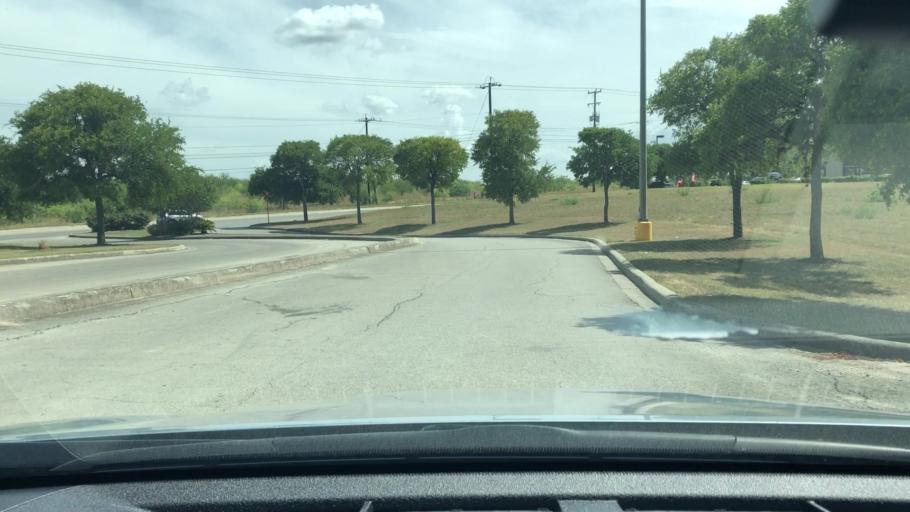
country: US
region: Texas
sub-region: Bexar County
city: Live Oak
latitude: 29.5938
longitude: -98.3498
